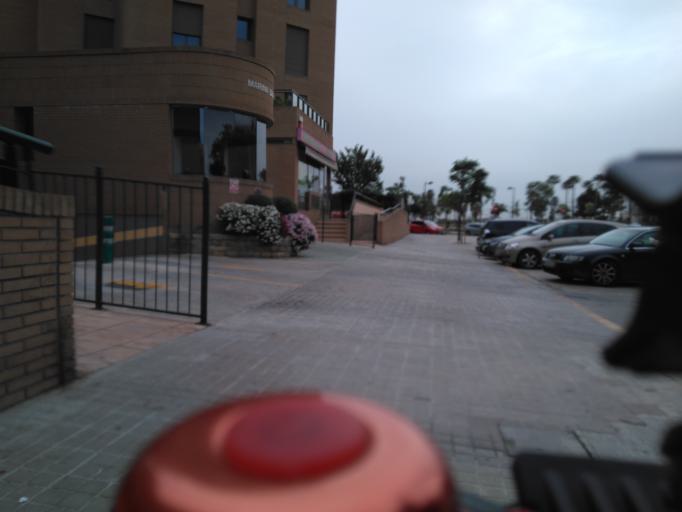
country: ES
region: Valencia
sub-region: Provincia de Valencia
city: Mislata
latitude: 39.4918
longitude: -0.4056
